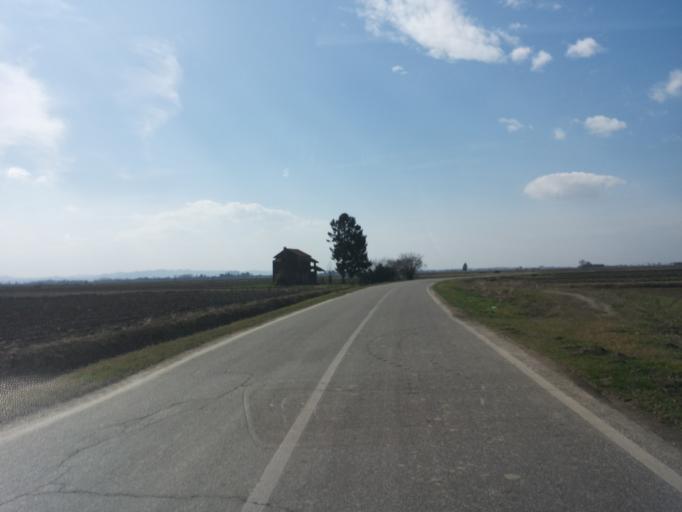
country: IT
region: Piedmont
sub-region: Provincia di Vercelli
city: Asigliano Vercellese
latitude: 45.2539
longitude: 8.3969
